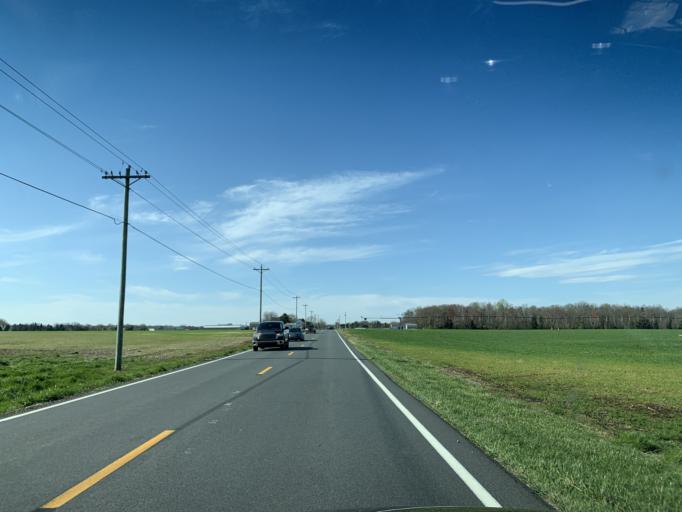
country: US
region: Delaware
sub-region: Kent County
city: Riverview
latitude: 39.0202
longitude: -75.5380
